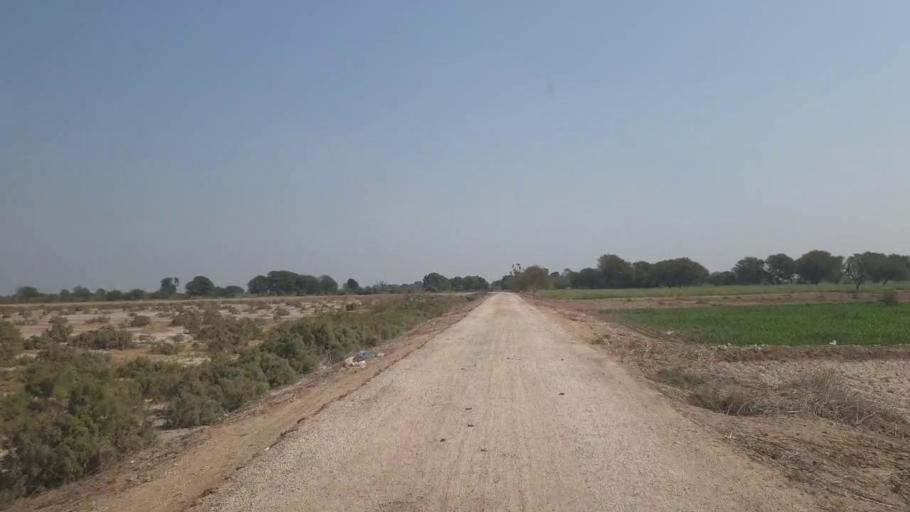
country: PK
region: Sindh
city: Mirpur Khas
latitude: 25.4420
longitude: 68.8856
